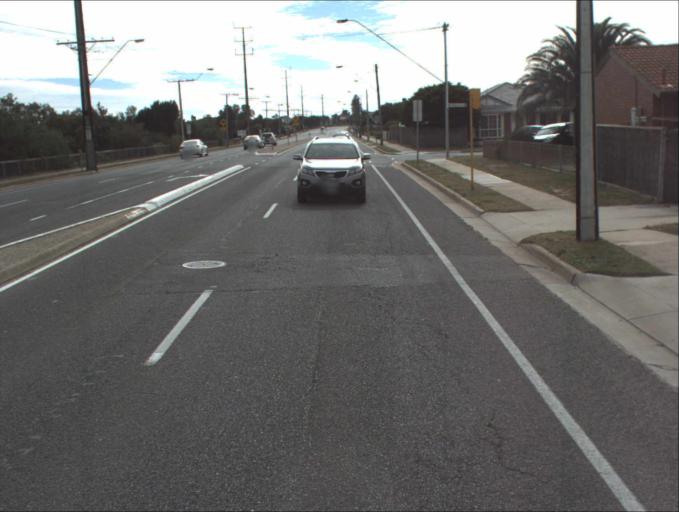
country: AU
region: South Australia
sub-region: Charles Sturt
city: West Lakes Shore
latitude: -34.8554
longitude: 138.4786
